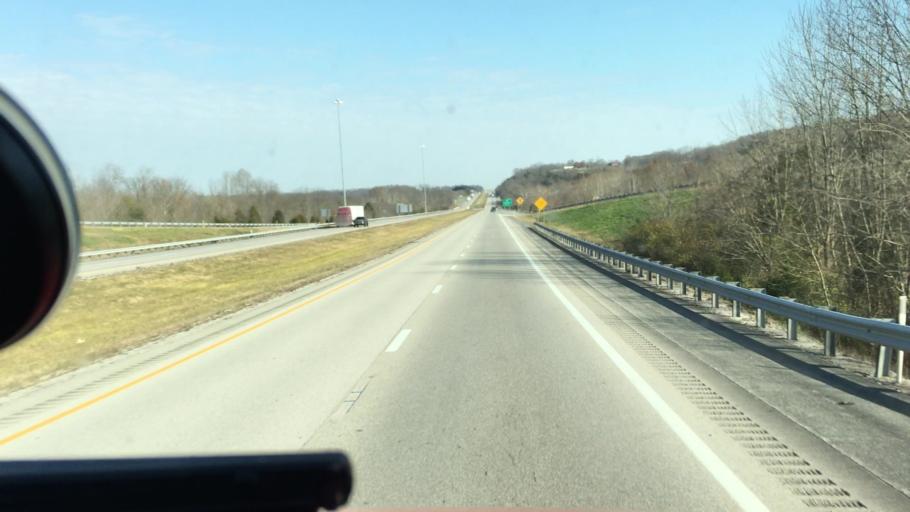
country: US
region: Kentucky
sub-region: Bath County
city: Owingsville
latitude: 38.1275
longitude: -83.7498
